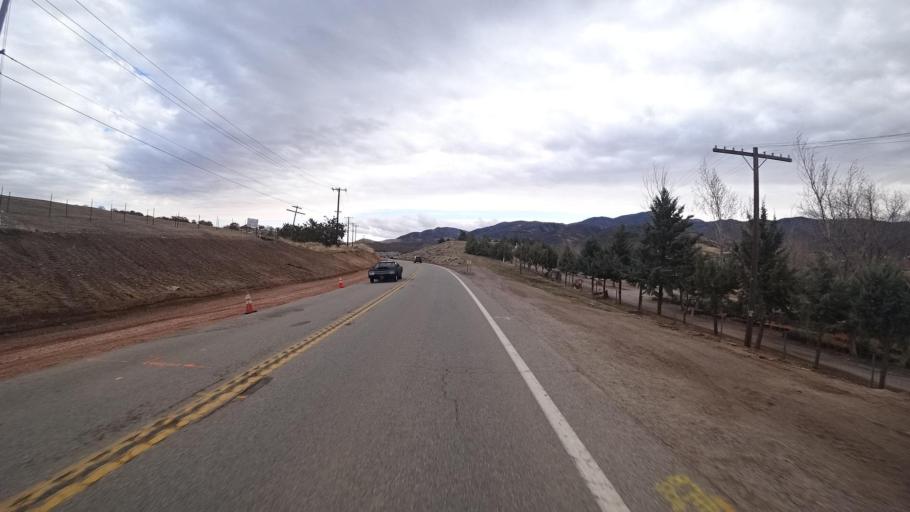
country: US
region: California
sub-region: Kern County
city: Golden Hills
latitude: 35.1152
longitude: -118.5304
